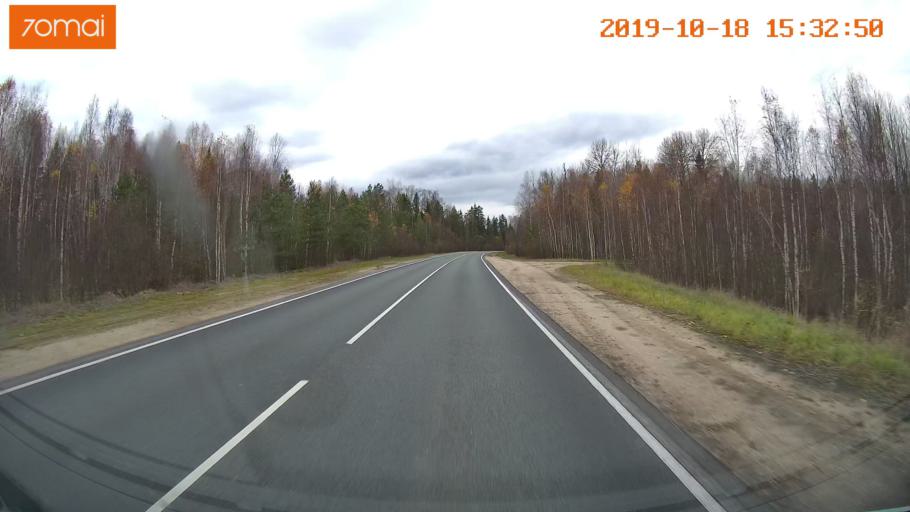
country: RU
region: Vladimir
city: Anopino
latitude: 55.8315
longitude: 40.6466
